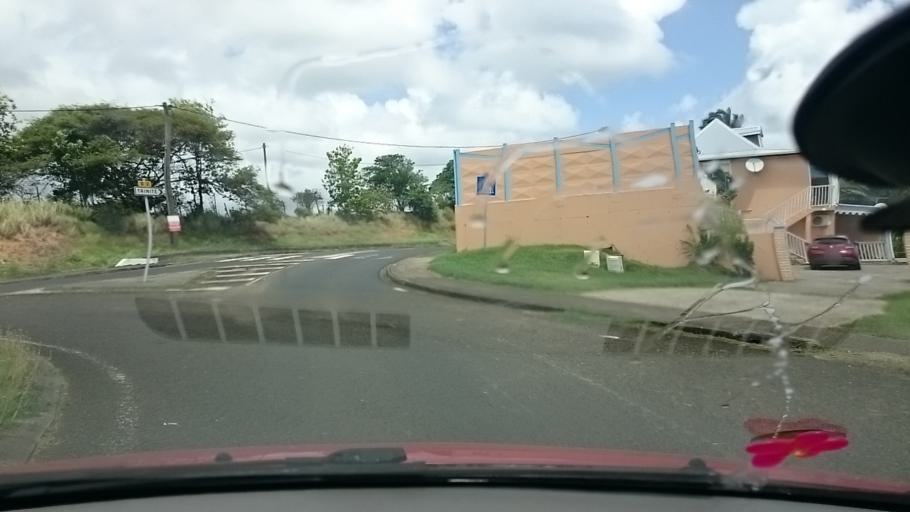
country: MQ
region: Martinique
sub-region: Martinique
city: La Trinite
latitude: 14.7550
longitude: -60.9244
